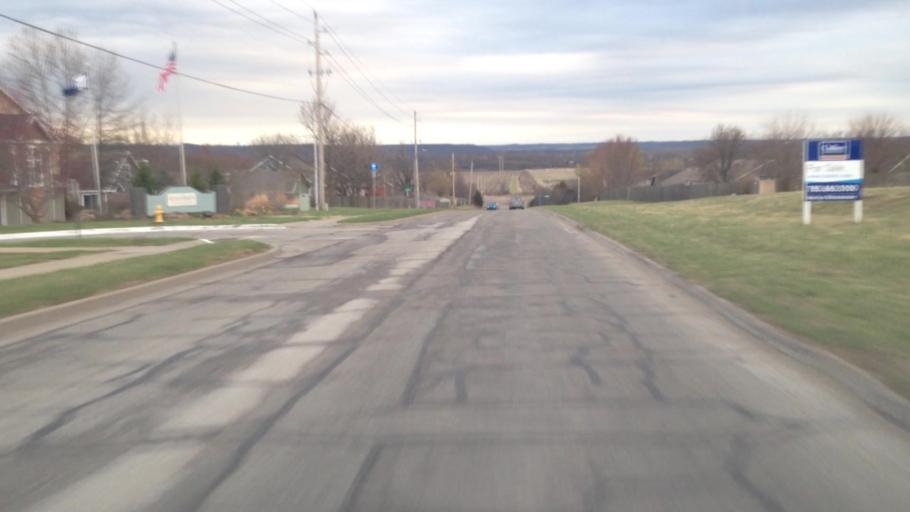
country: US
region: Kansas
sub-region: Douglas County
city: Lawrence
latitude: 38.9415
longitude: -95.3073
